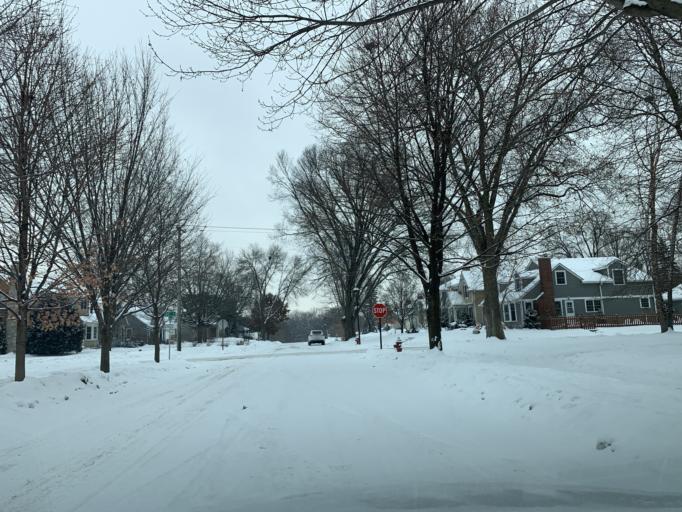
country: US
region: Minnesota
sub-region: Hennepin County
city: Saint Louis Park
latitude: 44.9310
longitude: -93.3367
